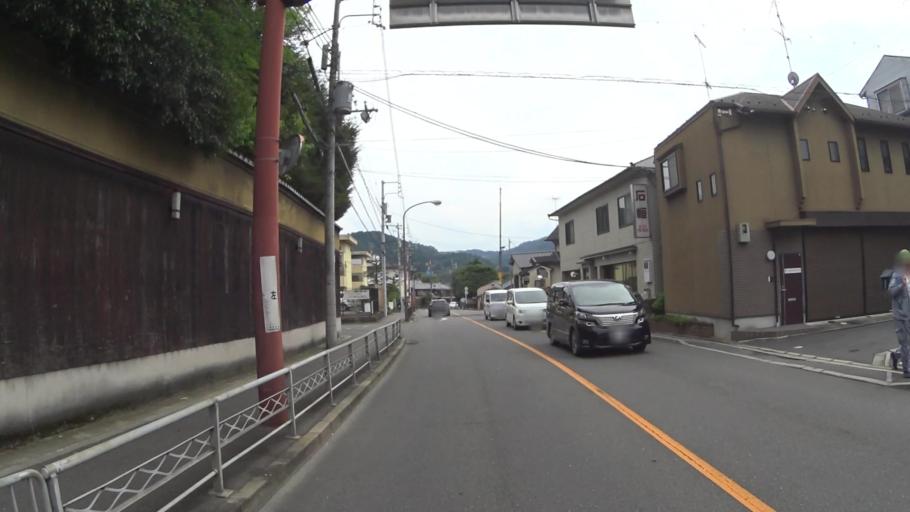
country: JP
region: Kyoto
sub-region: Kyoto-shi
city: Kamigyo-ku
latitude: 35.0163
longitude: 135.7908
